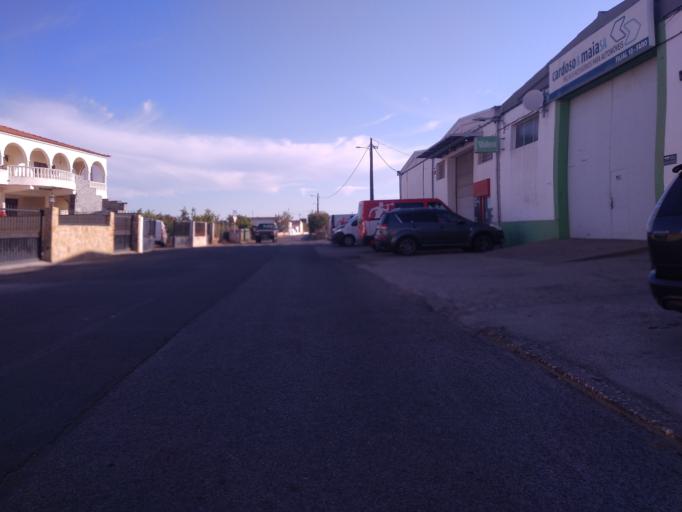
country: PT
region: Faro
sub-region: Faro
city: Faro
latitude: 37.0501
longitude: -7.9375
